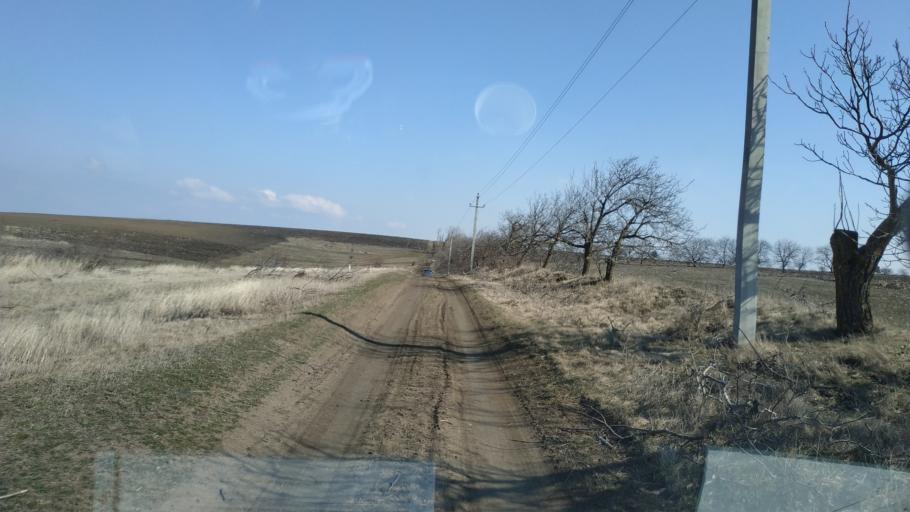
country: MD
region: Causeni
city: Causeni
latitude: 46.5542
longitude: 29.2735
